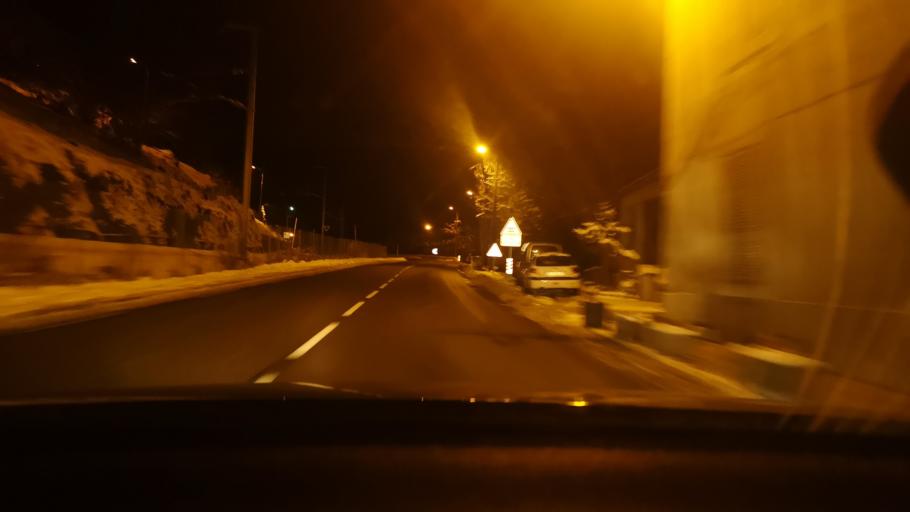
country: FR
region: Rhone-Alpes
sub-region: Departement de l'Ain
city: Chatillon-en-Michaille
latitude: 46.1770
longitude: 5.7378
